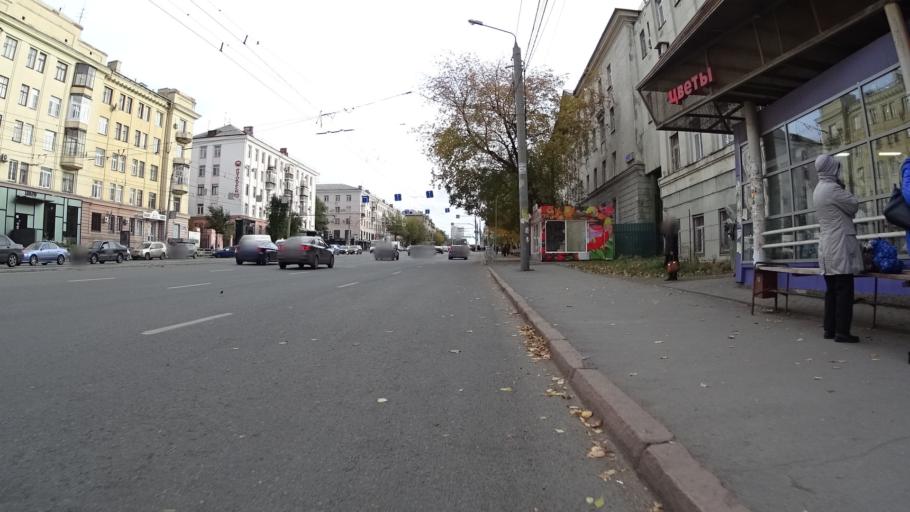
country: RU
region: Chelyabinsk
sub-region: Gorod Chelyabinsk
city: Chelyabinsk
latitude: 55.1592
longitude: 61.3888
